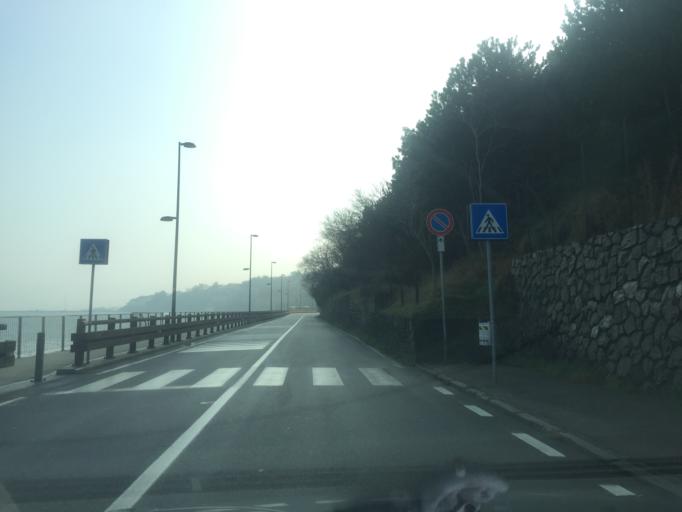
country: IT
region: Friuli Venezia Giulia
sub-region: Provincia di Trieste
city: Muggia
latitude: 45.6103
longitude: 13.7374
